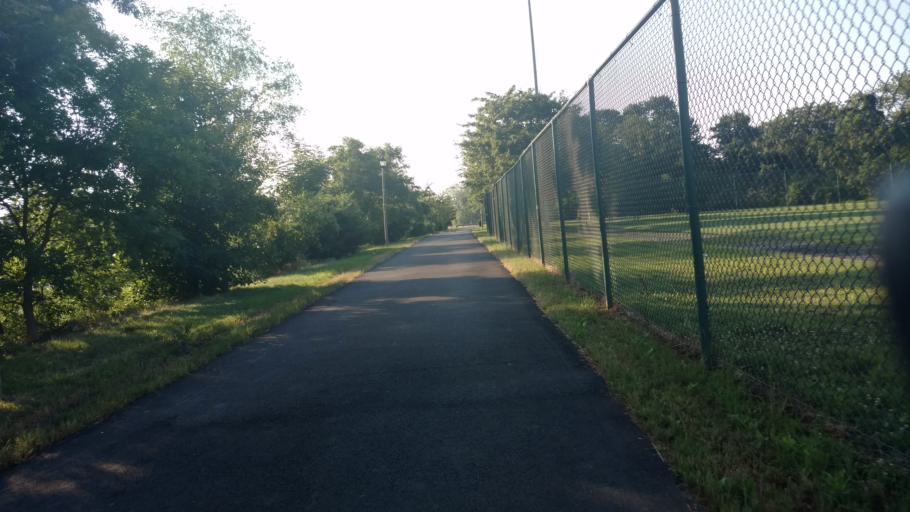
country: US
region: Virginia
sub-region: City of Alexandria
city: Alexandria
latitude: 38.8437
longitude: -77.0624
